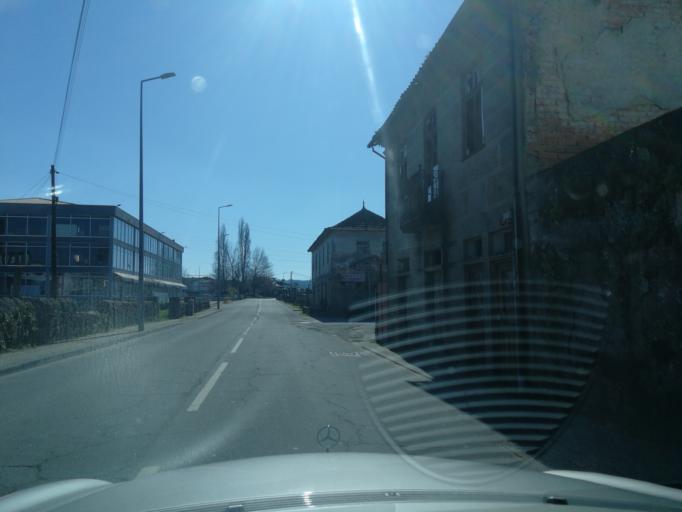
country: PT
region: Braga
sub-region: Vila Nova de Famalicao
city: Vila Nova de Famalicao
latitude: 41.3976
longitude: -8.5207
